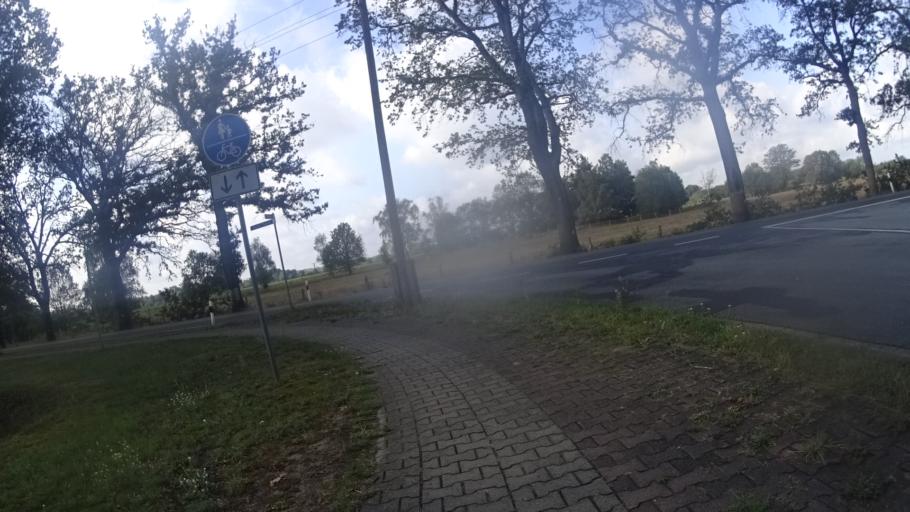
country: DE
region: Brandenburg
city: Wittenberge
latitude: 53.0071
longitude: 11.7159
